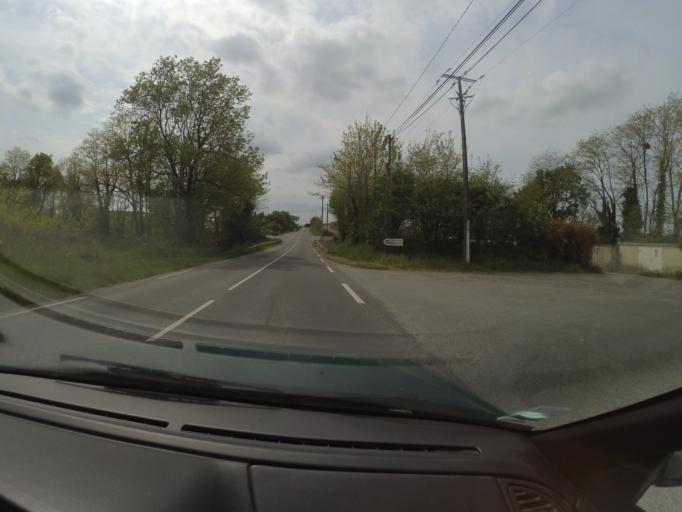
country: FR
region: Pays de la Loire
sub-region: Departement de la Loire-Atlantique
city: Gorges
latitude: 47.1024
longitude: -1.3124
